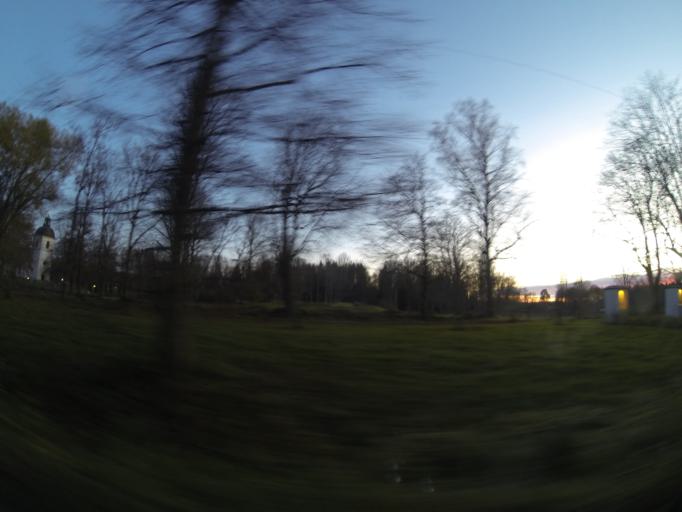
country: SE
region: OErebro
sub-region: Lindesbergs Kommun
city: Fellingsbro
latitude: 59.3261
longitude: 15.4743
